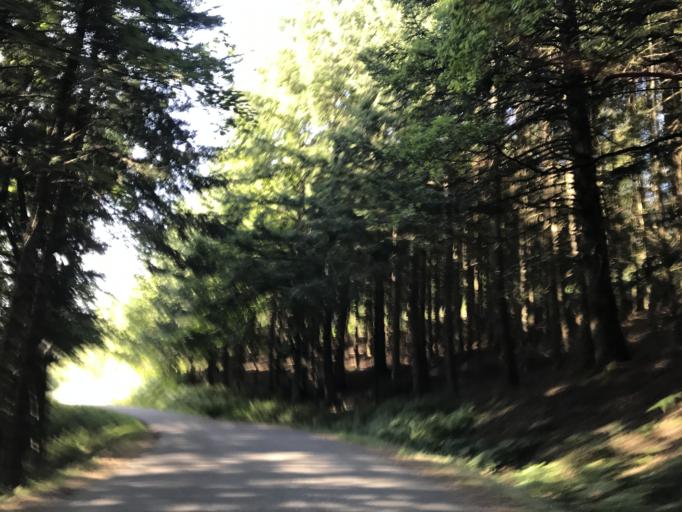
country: FR
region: Auvergne
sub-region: Departement du Puy-de-Dome
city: Job
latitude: 45.6737
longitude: 3.7365
